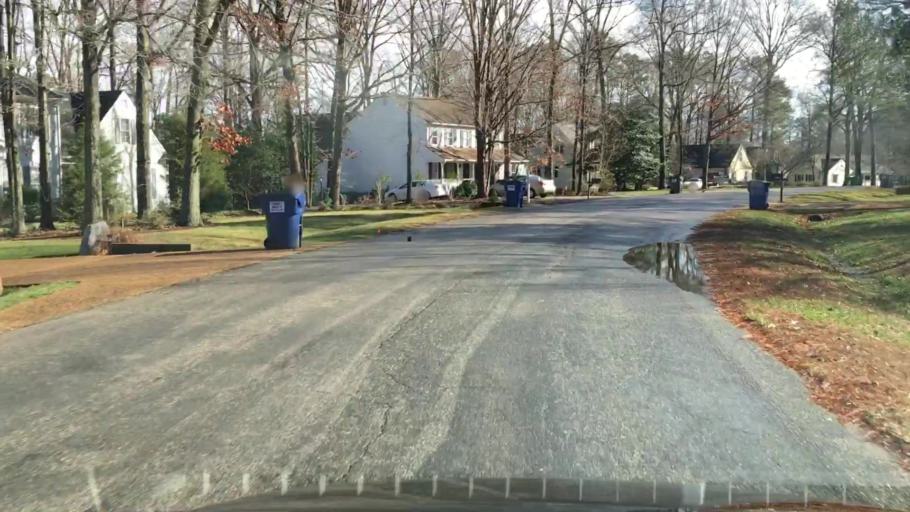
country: US
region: Virginia
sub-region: Chesterfield County
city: Bon Air
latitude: 37.5347
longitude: -77.6061
